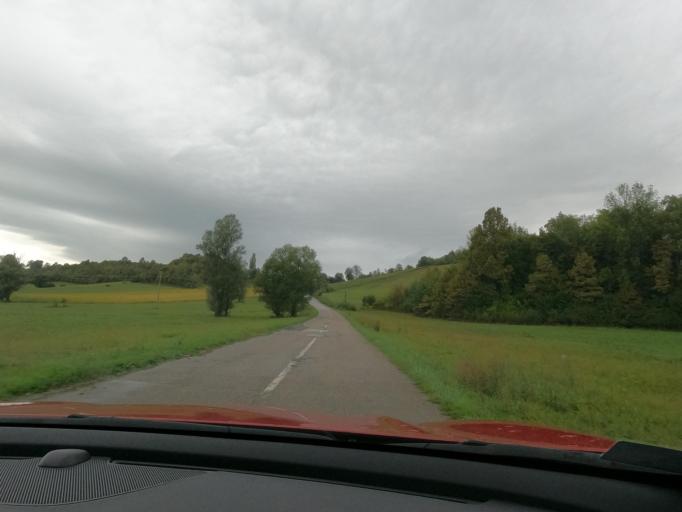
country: HR
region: Sisacko-Moslavacka
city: Glina
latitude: 45.3048
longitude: 16.1748
